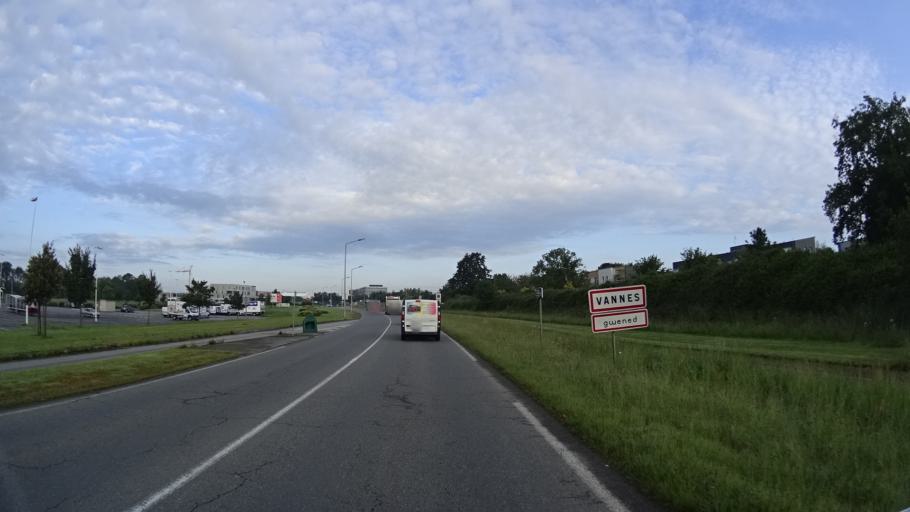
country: FR
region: Brittany
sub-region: Departement du Morbihan
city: Vannes
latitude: 47.6441
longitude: -2.7400
